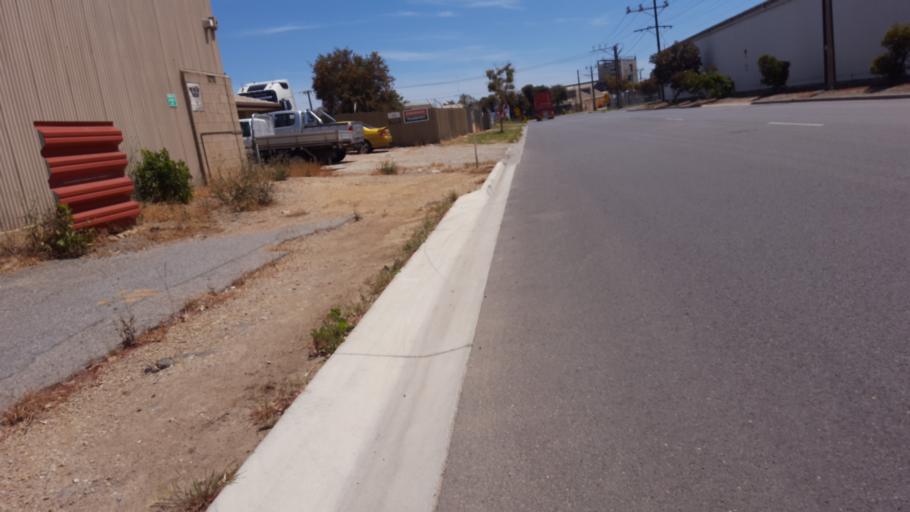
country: AU
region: South Australia
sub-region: Port Adelaide Enfield
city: Alberton
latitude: -34.8450
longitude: 138.5210
